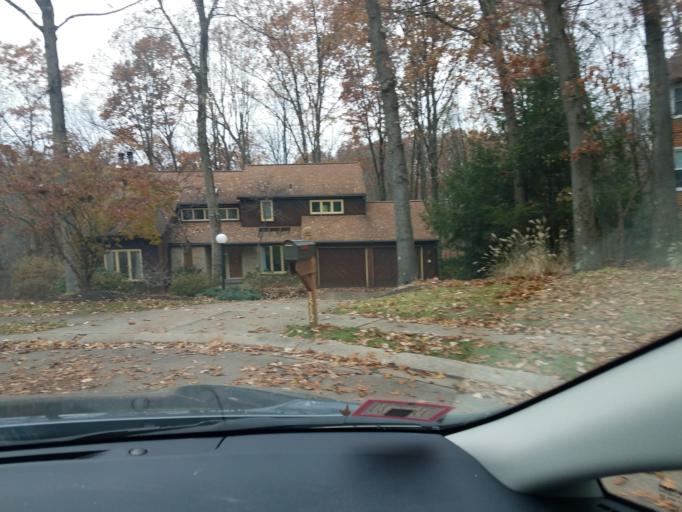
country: US
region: Pennsylvania
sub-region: Allegheny County
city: Franklin Park
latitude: 40.5571
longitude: -80.0674
